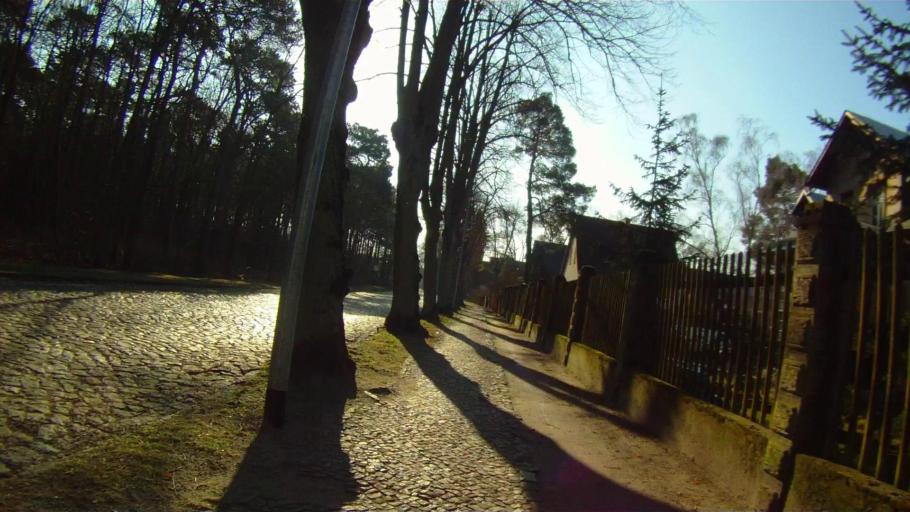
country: DE
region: Brandenburg
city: Schoneiche
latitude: 52.4617
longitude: 13.7027
